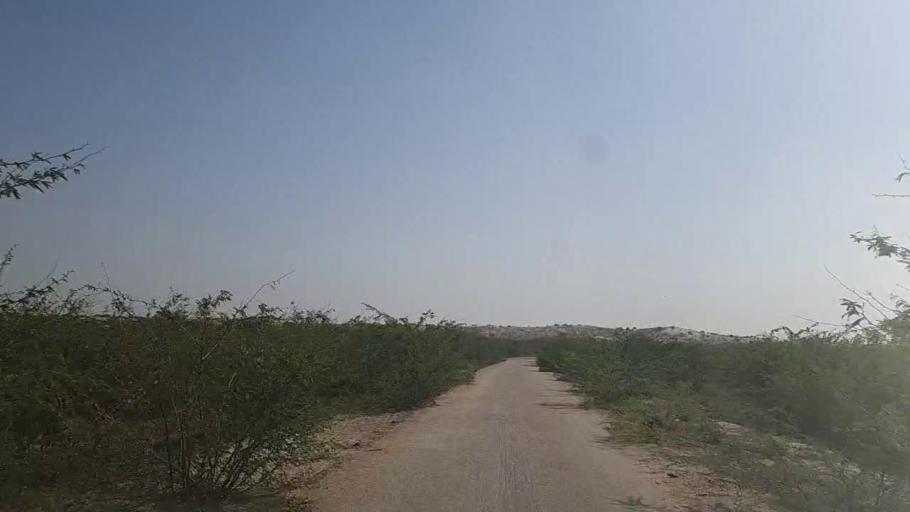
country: PK
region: Sindh
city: Naukot
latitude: 24.5758
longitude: 69.2938
